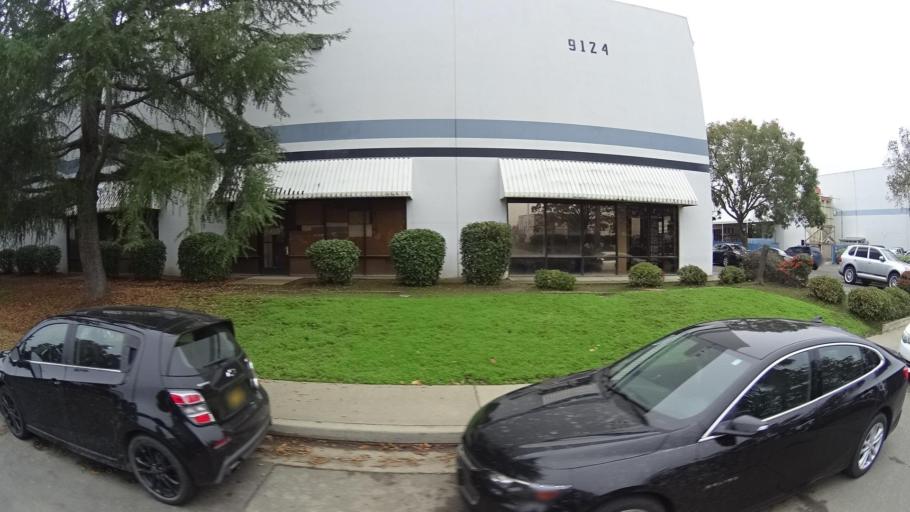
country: US
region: California
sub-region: Sacramento County
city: Elk Grove
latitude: 38.3839
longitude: -121.3616
